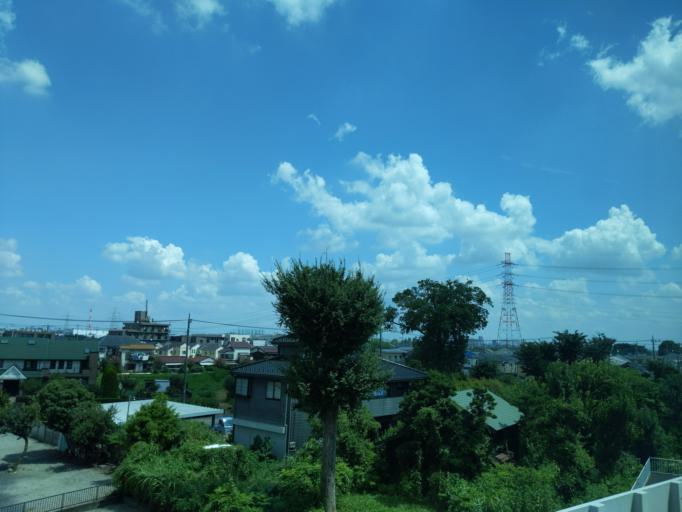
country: JP
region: Tokyo
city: Chofugaoka
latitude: 35.6482
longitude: 139.4946
